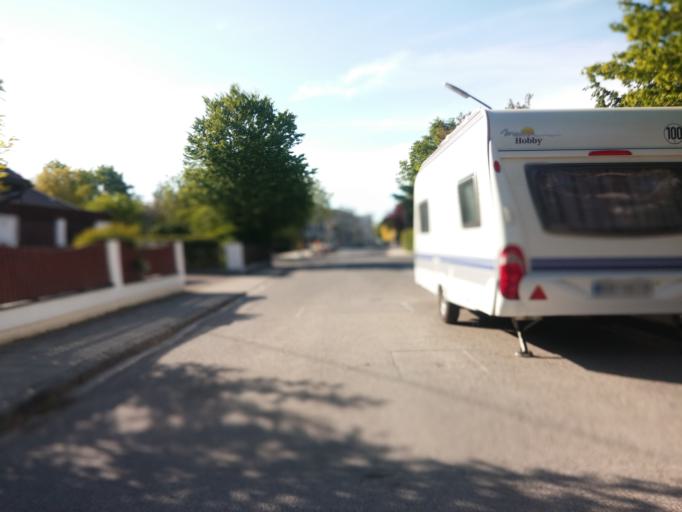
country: DE
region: Bavaria
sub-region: Upper Bavaria
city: Vaterstetten
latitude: 48.1109
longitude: 11.7709
